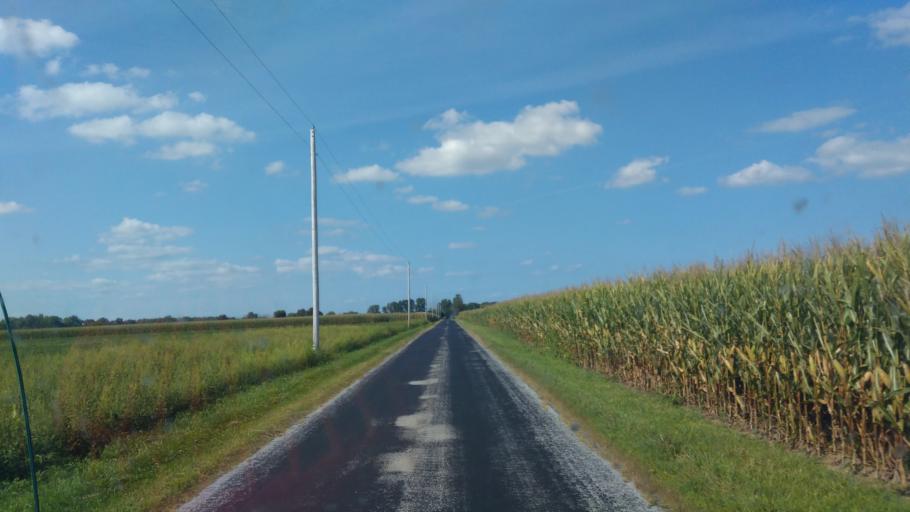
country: US
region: Ohio
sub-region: Hardin County
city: Forest
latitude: 40.7034
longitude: -83.4780
